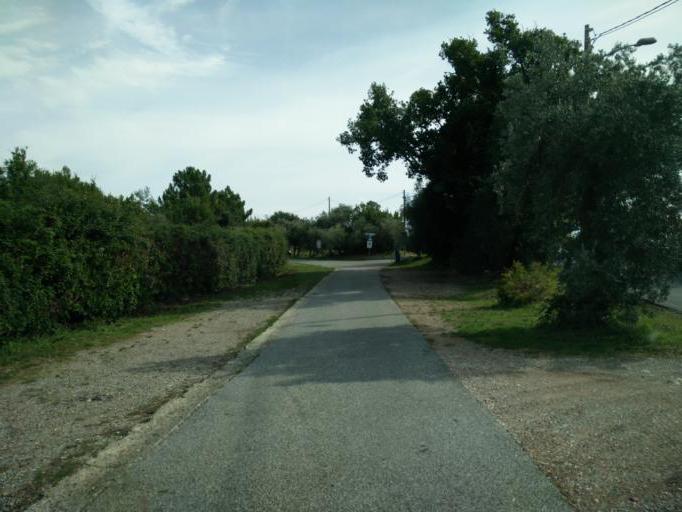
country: IT
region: Liguria
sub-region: Provincia di La Spezia
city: Le Grazie
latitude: 44.0599
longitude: 9.8463
